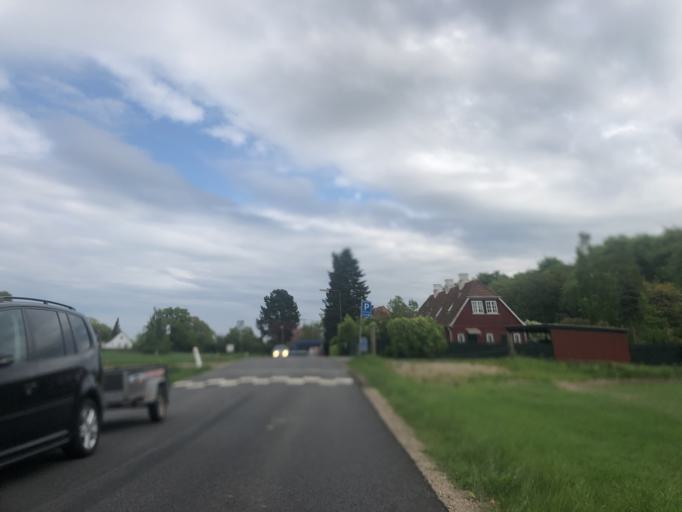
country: DK
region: Zealand
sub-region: Koge Kommune
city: Koge
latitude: 55.4697
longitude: 12.1529
